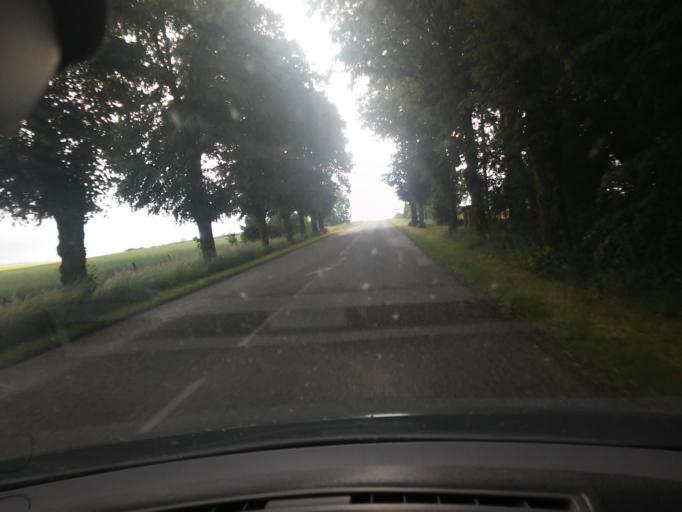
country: FR
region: Lorraine
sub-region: Departement de Meurthe-et-Moselle
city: Doncourt-les-Conflans
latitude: 49.0939
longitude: 5.9540
